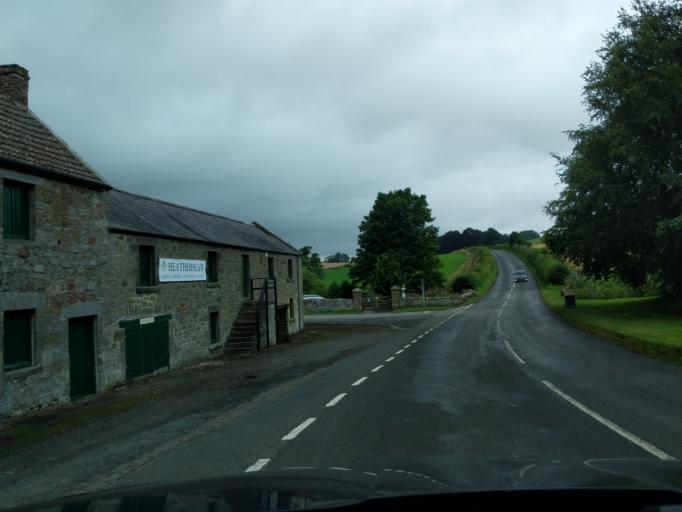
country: GB
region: England
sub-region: Northumberland
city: Ford
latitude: 55.6396
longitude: -2.1064
